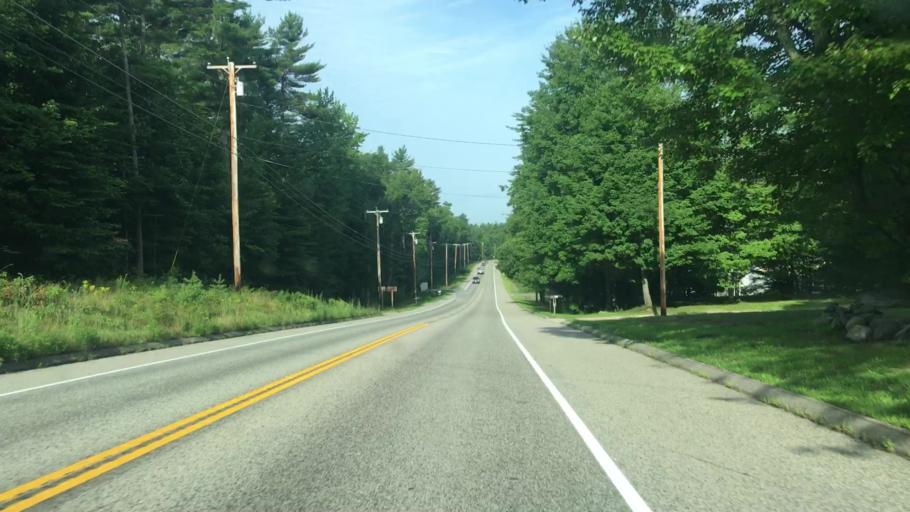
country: US
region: Maine
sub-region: Cumberland County
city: Steep Falls
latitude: 43.7323
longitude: -70.5780
